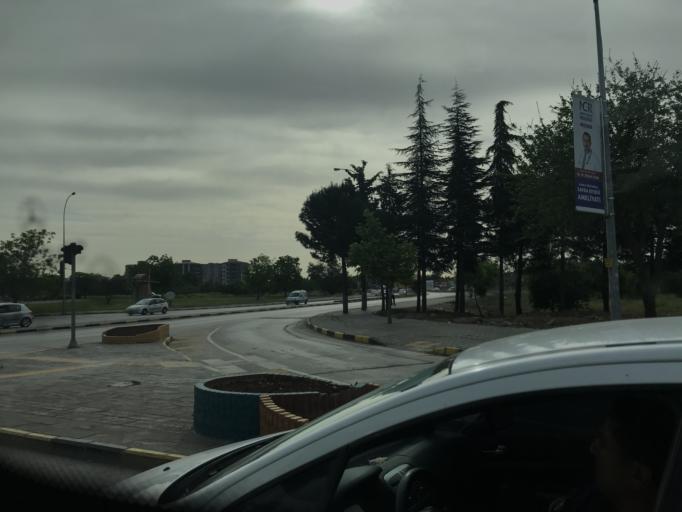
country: TR
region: Gaziantep
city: Sahinbey
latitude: 37.0623
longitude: 37.3345
